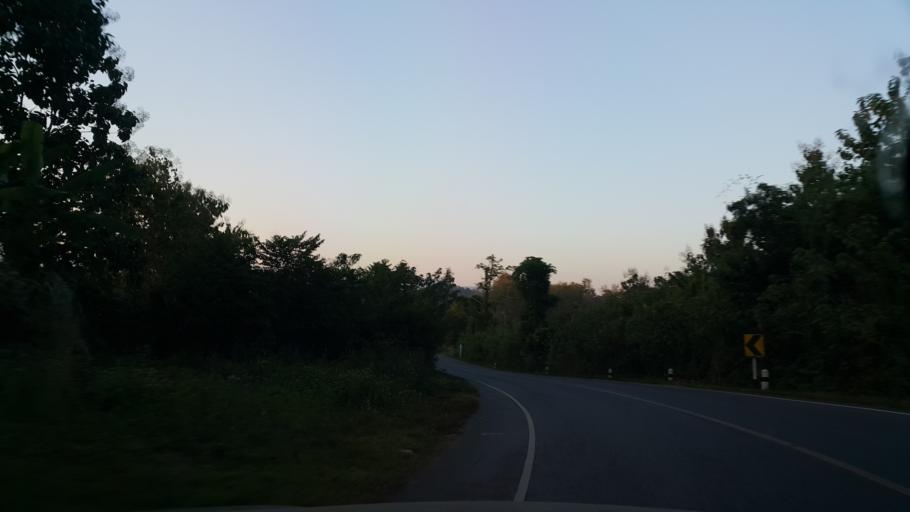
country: TH
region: Phrae
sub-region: Amphoe Wang Chin
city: Wang Chin
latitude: 17.8346
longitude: 99.6421
